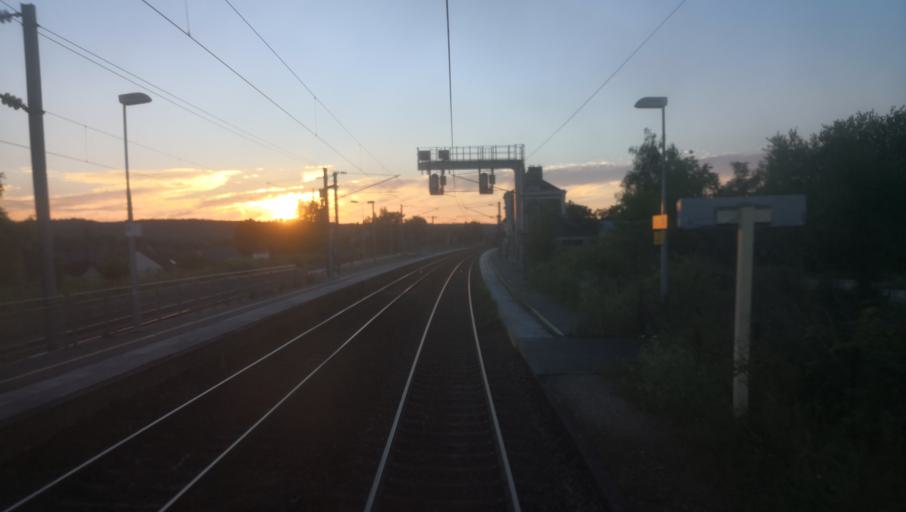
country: FR
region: Haute-Normandie
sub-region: Departement de l'Eure
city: Bueil
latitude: 48.9245
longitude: 1.4444
